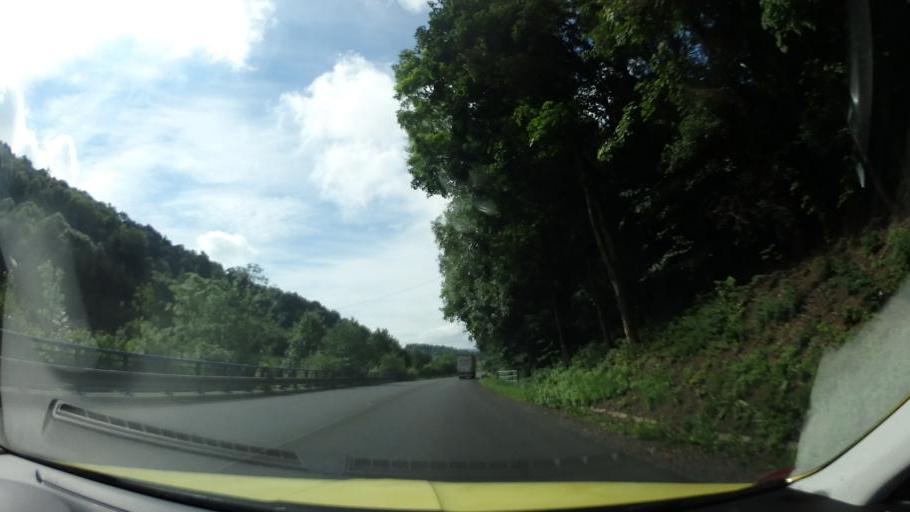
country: CZ
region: Moravskoslezsky
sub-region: Okres Novy Jicin
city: Novy Jicin
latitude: 49.5698
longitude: 18.0248
